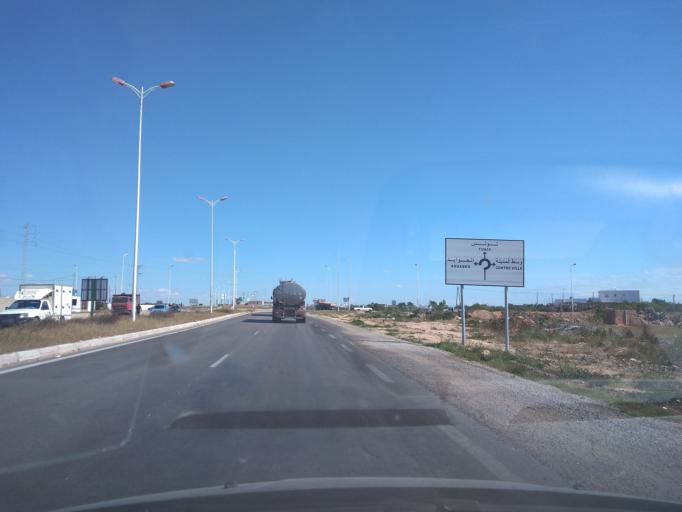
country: TN
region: Safaqis
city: Sfax
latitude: 34.8017
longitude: 10.6879
